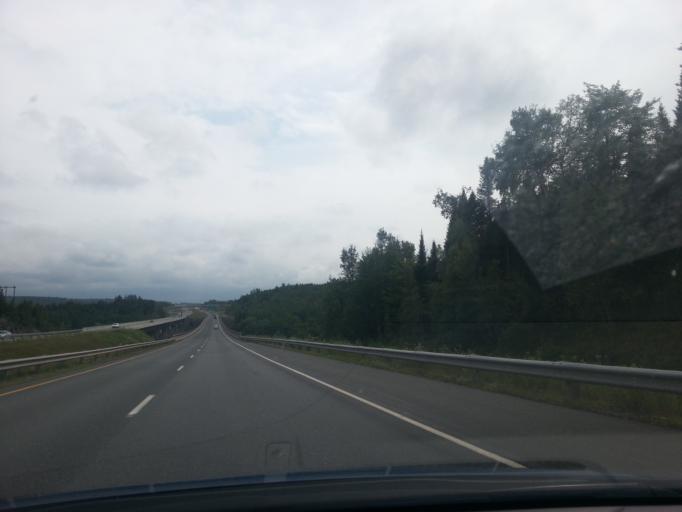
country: US
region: Maine
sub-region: Aroostook County
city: Houlton
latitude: 46.1654
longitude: -67.6080
